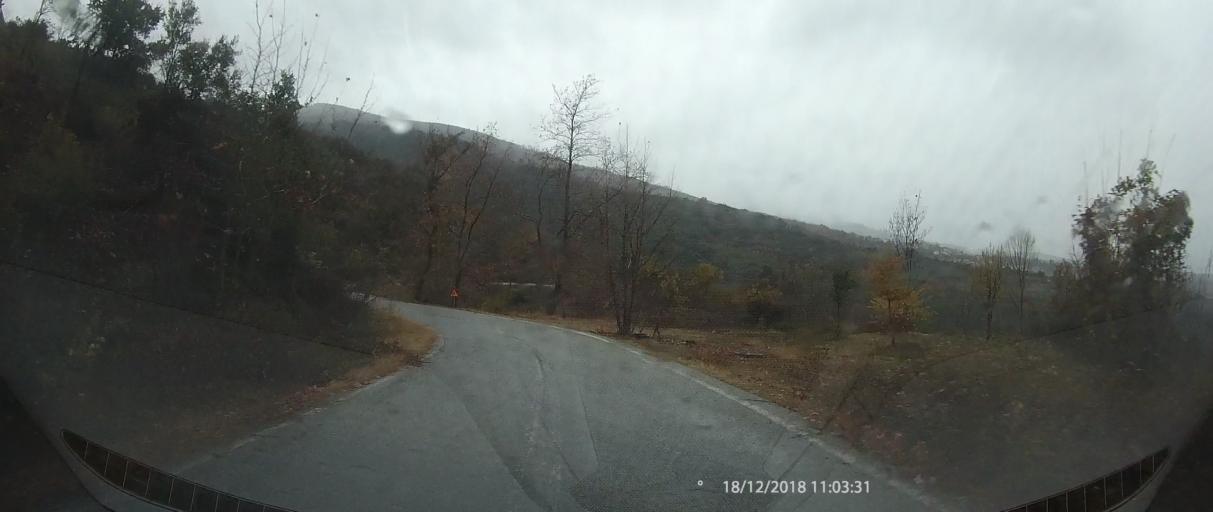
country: GR
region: Central Macedonia
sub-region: Nomos Pierias
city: Kato Milia
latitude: 40.2087
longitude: 22.3166
